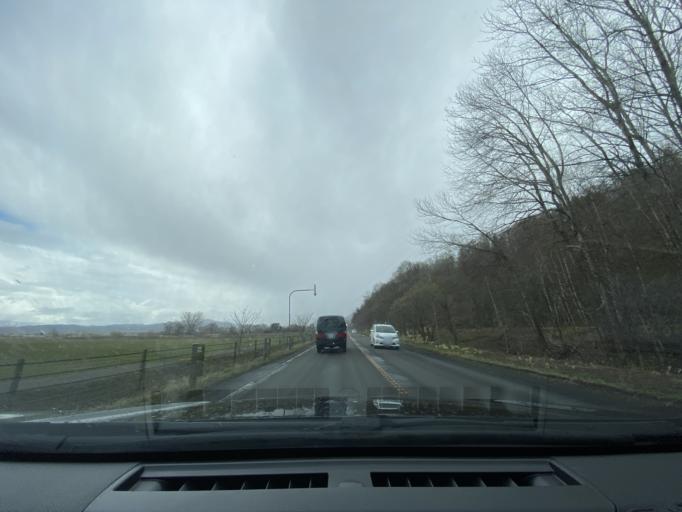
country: JP
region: Hokkaido
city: Fukagawa
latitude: 43.7041
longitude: 142.0896
